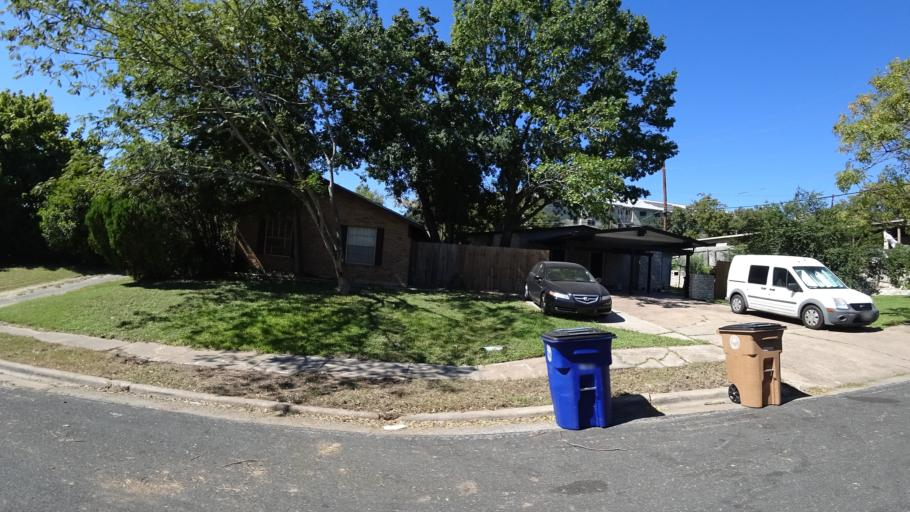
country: US
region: Texas
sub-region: Travis County
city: Austin
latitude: 30.2307
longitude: -97.7408
